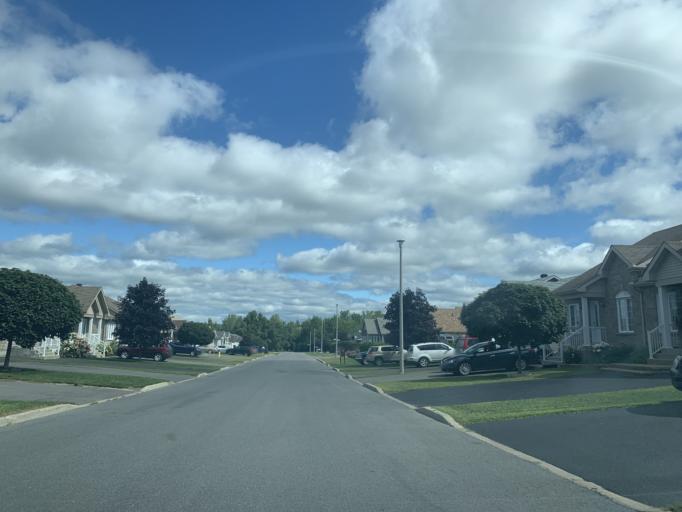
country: CA
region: Ontario
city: Hawkesbury
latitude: 45.6021
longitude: -74.5816
